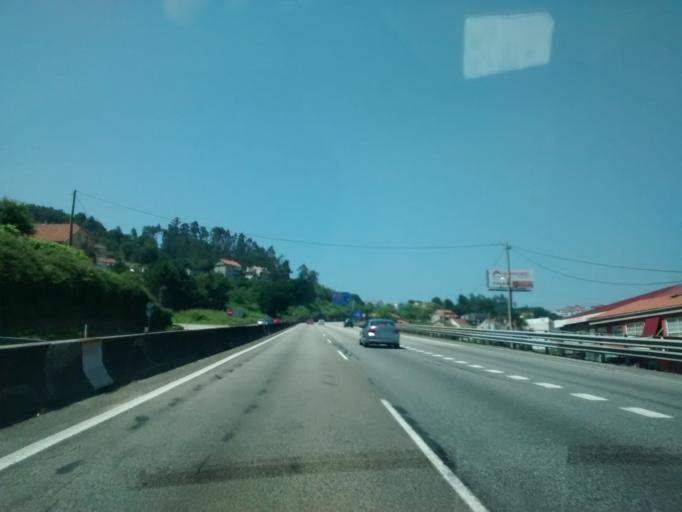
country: ES
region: Galicia
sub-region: Provincia de Pontevedra
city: Porrino
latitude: 42.1993
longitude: -8.6567
